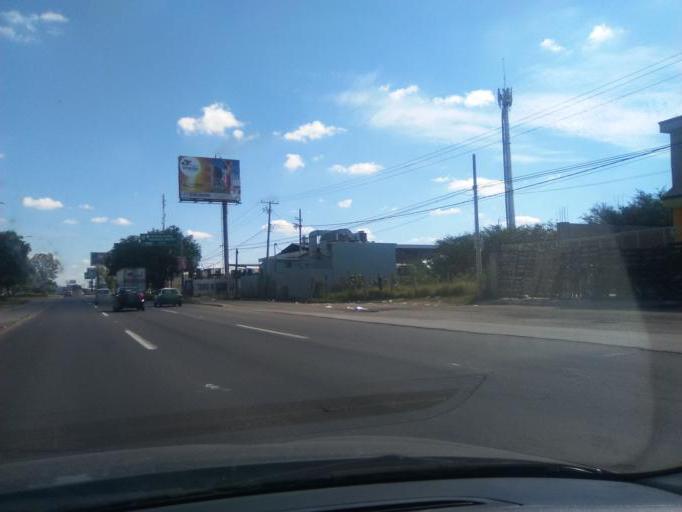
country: MX
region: Guanajuato
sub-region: Leon
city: Ladrilleras del Refugio
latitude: 21.0689
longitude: -101.5942
